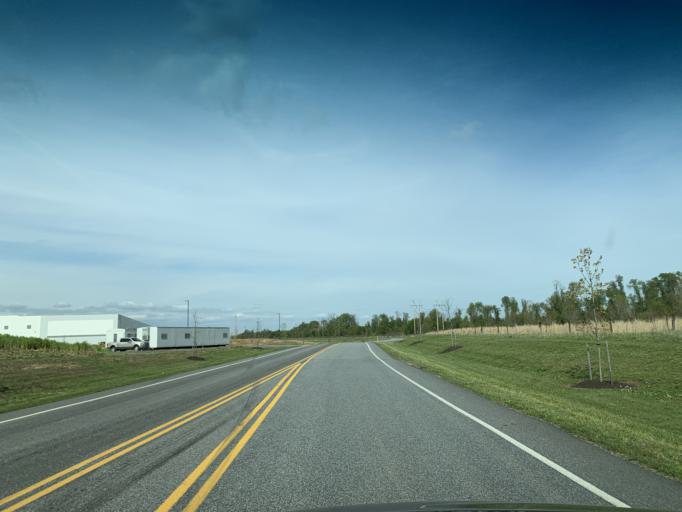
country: US
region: Maryland
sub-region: Harford County
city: Perryman
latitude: 39.4656
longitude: -76.1965
